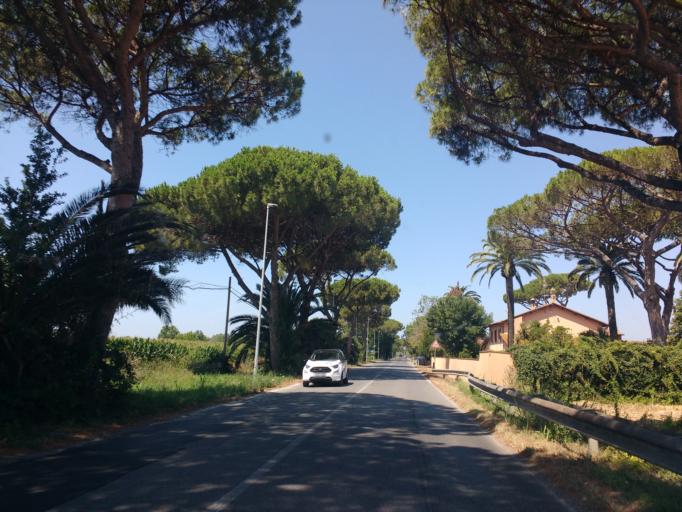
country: IT
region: Latium
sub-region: Citta metropolitana di Roma Capitale
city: Maccarese
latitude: 41.8782
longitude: 12.2078
